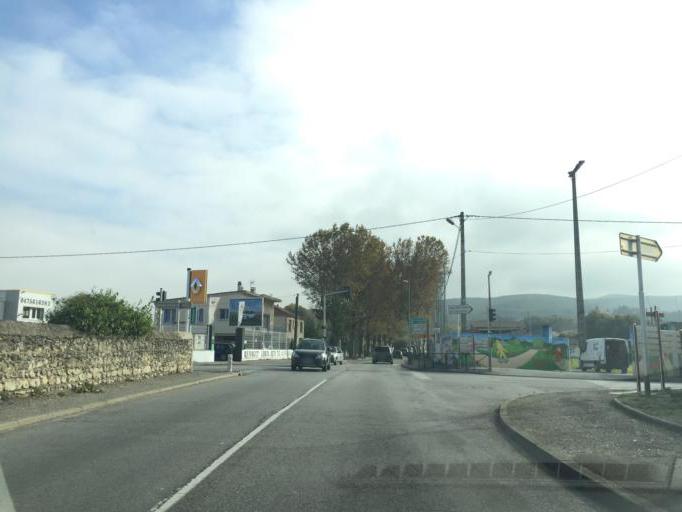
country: FR
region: Rhone-Alpes
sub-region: Departement de la Drome
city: Loriol-sur-Drome
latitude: 44.7544
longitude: 4.8138
